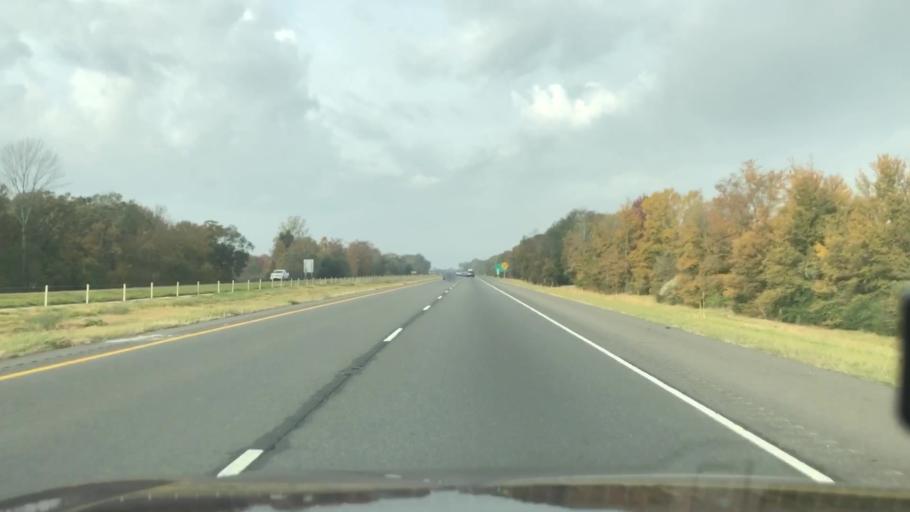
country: US
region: Louisiana
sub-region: Richland Parish
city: Delhi
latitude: 32.4542
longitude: -91.6010
